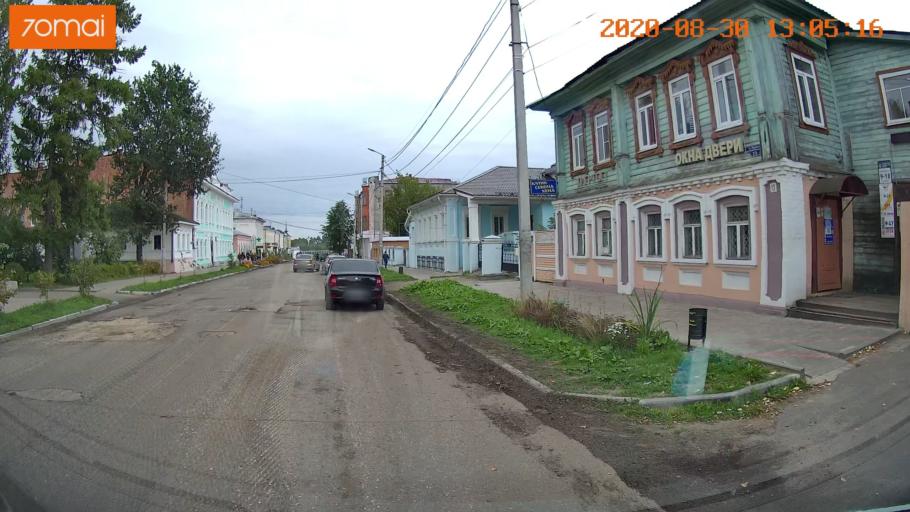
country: RU
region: Ivanovo
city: Kineshma
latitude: 57.4435
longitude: 42.1654
